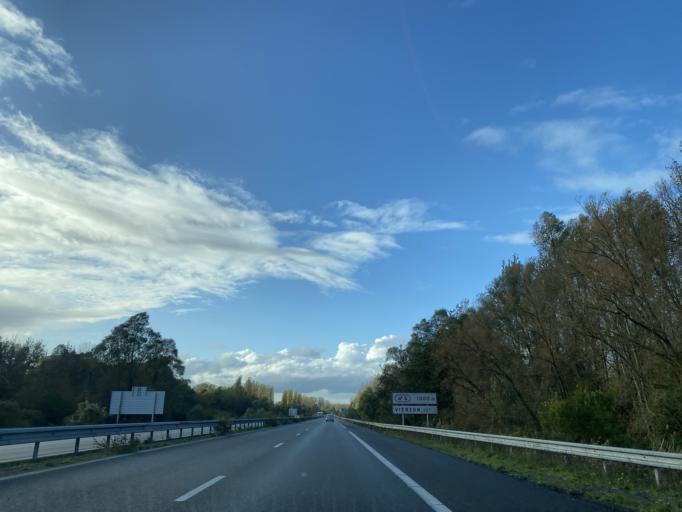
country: FR
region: Centre
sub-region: Departement du Cher
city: Foecy
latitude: 47.2014
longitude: 2.1351
